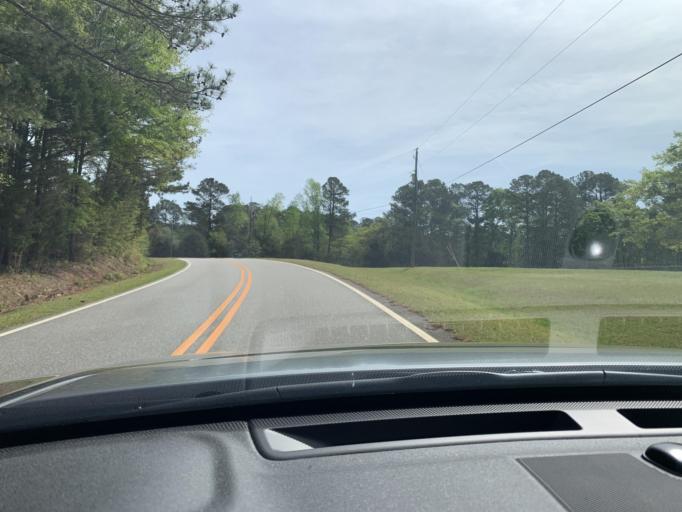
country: US
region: Georgia
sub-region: Oconee County
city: Watkinsville
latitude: 33.8447
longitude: -83.4719
